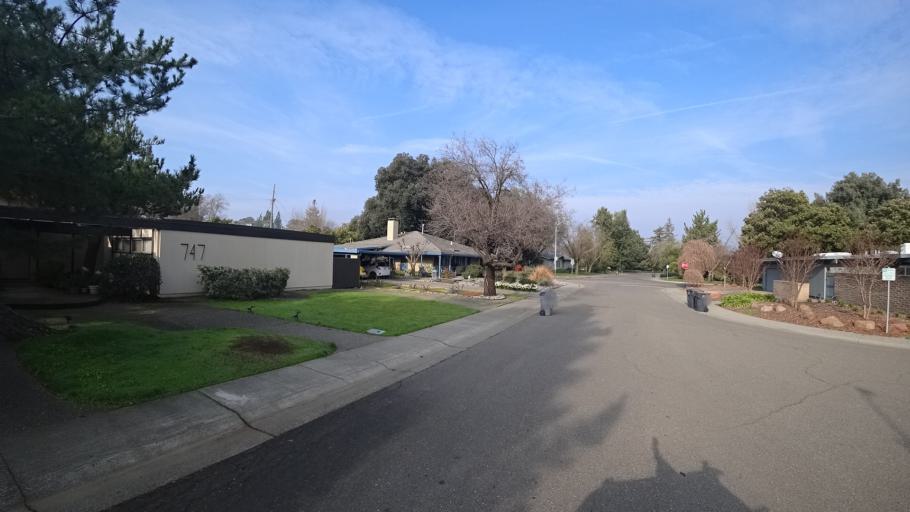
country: US
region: California
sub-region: Yolo County
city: Davis
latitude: 38.5498
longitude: -121.7647
